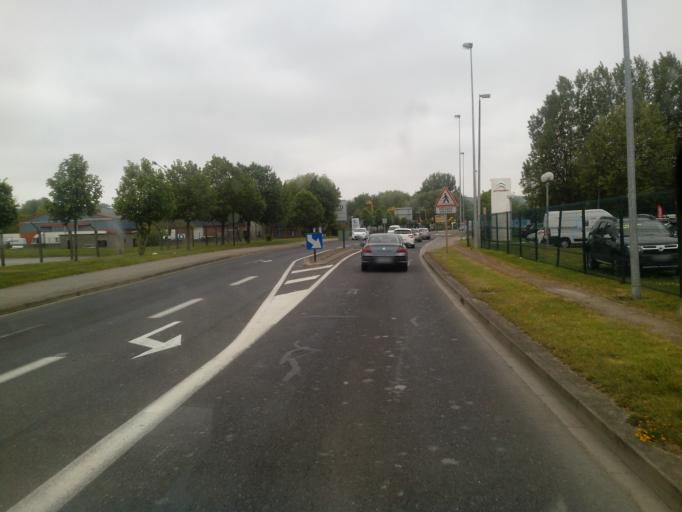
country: FR
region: Nord-Pas-de-Calais
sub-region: Departement du Pas-de-Calais
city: Saint-Leonard
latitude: 50.6874
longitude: 1.6229
